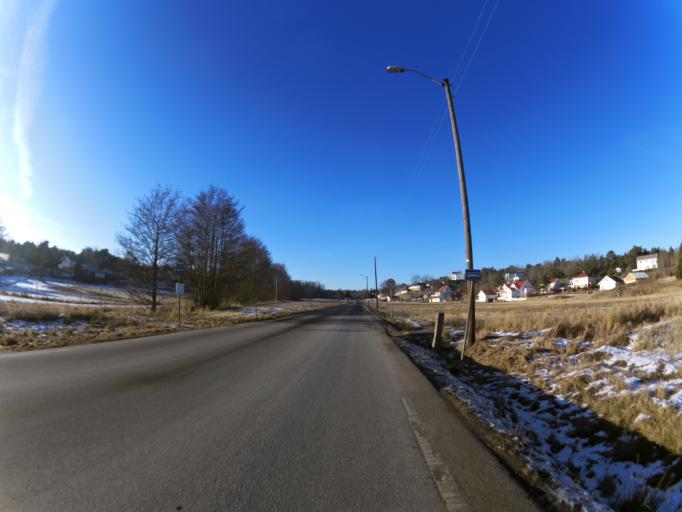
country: NO
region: Ostfold
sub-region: Fredrikstad
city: Lervik
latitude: 59.1975
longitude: 10.8210
